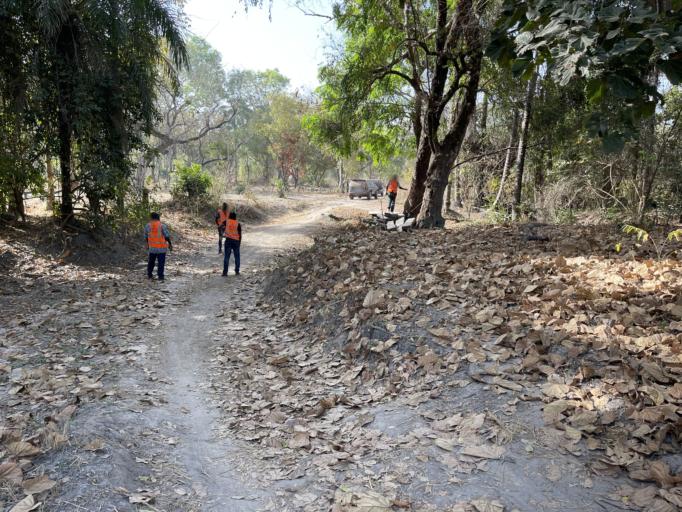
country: GW
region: Oio
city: Farim
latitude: 12.4750
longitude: -15.4067
